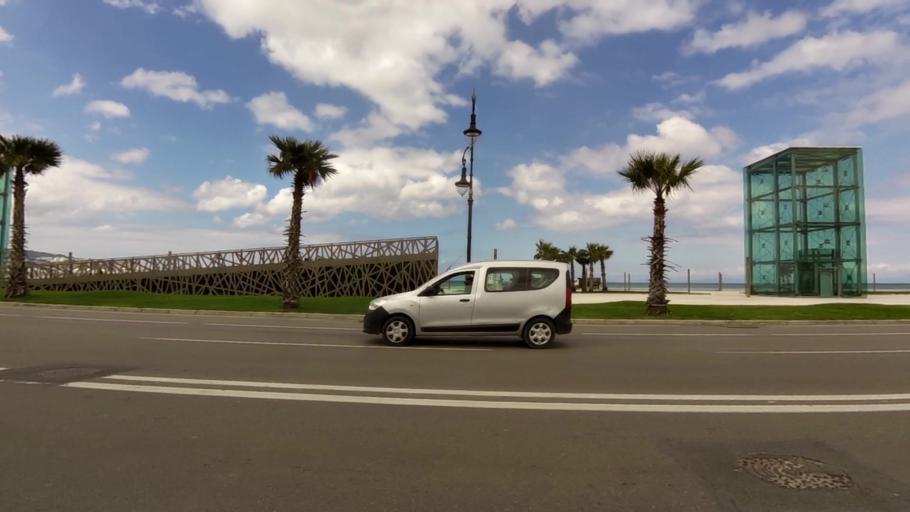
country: MA
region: Tanger-Tetouan
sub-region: Tanger-Assilah
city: Tangier
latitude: 35.7775
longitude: -5.7772
